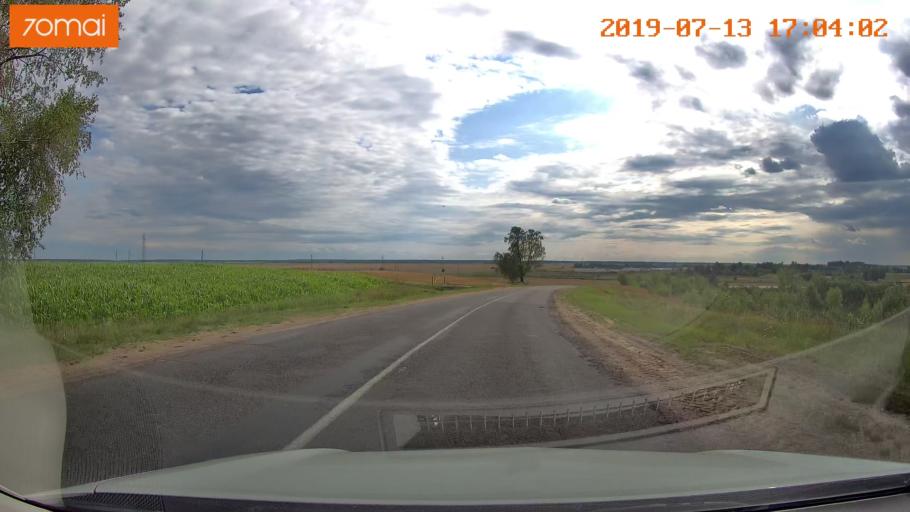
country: BY
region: Mogilev
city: Kirawsk
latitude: 53.2718
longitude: 29.3729
